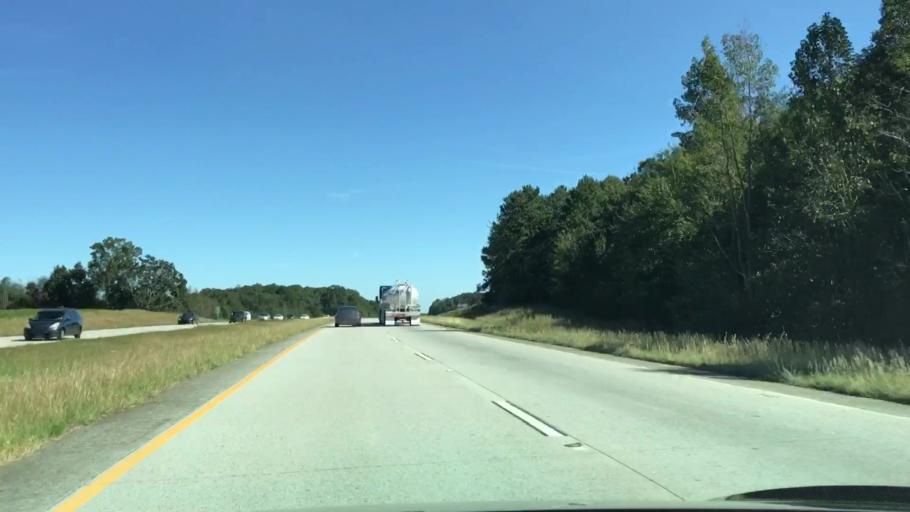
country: US
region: Georgia
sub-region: Oconee County
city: Bogart
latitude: 33.9417
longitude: -83.5598
